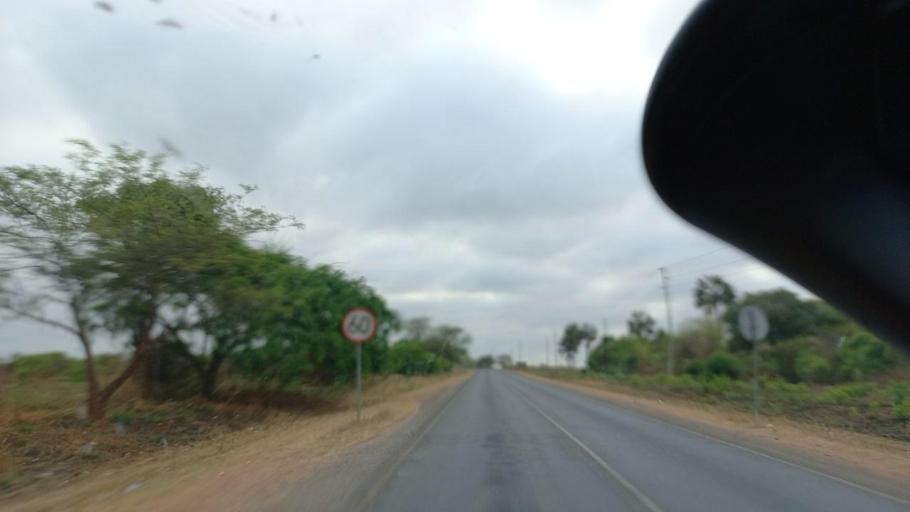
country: ZM
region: Lusaka
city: Chongwe
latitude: -15.3472
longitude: 28.5791
